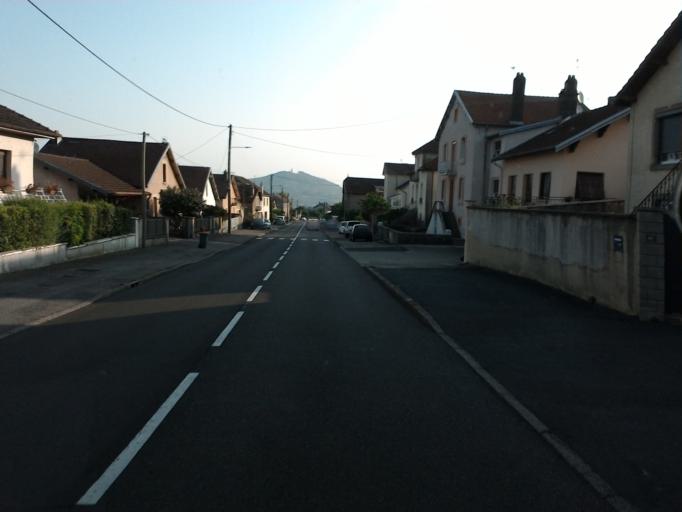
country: FR
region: Franche-Comte
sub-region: Departement de la Haute-Saone
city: Echenoz-la-Meline
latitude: 47.6052
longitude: 6.1426
